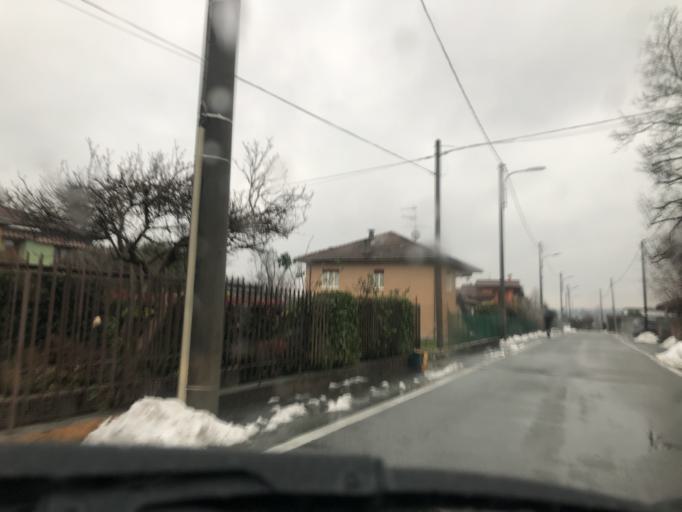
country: IT
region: Piedmont
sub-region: Provincia di Novara
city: Oleggio Castello
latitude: 45.7548
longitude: 8.5262
